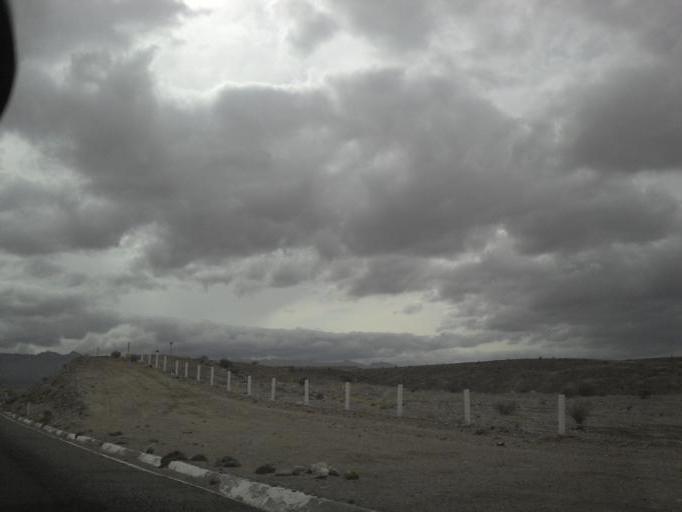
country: MX
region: Baja California
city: Progreso
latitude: 32.5647
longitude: -115.8649
